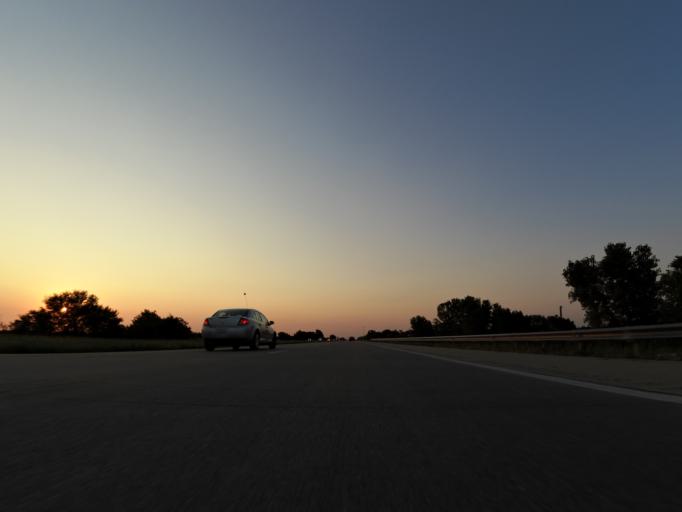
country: US
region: Kansas
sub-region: Reno County
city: Haven
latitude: 37.9224
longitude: -97.8349
